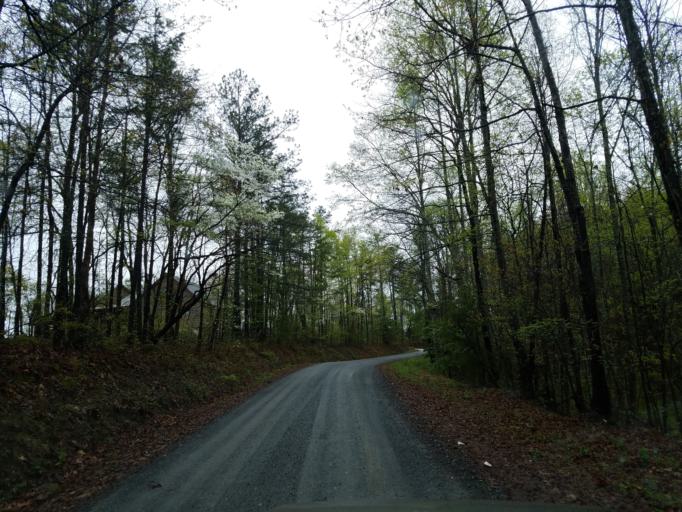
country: US
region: Georgia
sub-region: Pickens County
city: Jasper
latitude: 34.5494
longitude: -84.5236
